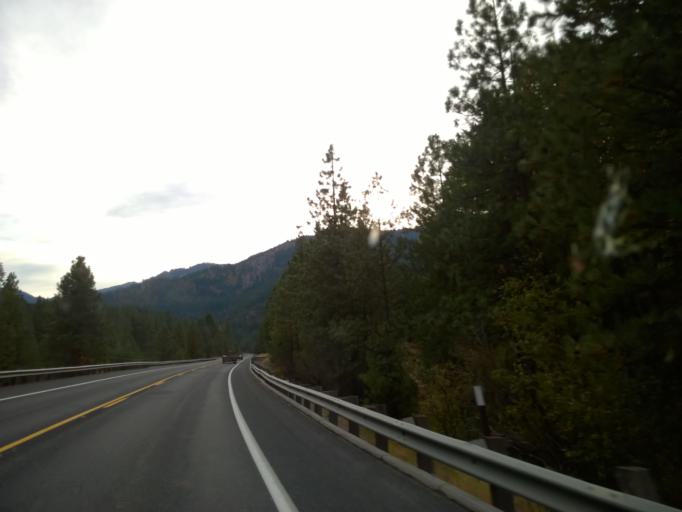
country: US
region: Washington
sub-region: Chelan County
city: Leavenworth
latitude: 47.4914
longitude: -120.6388
